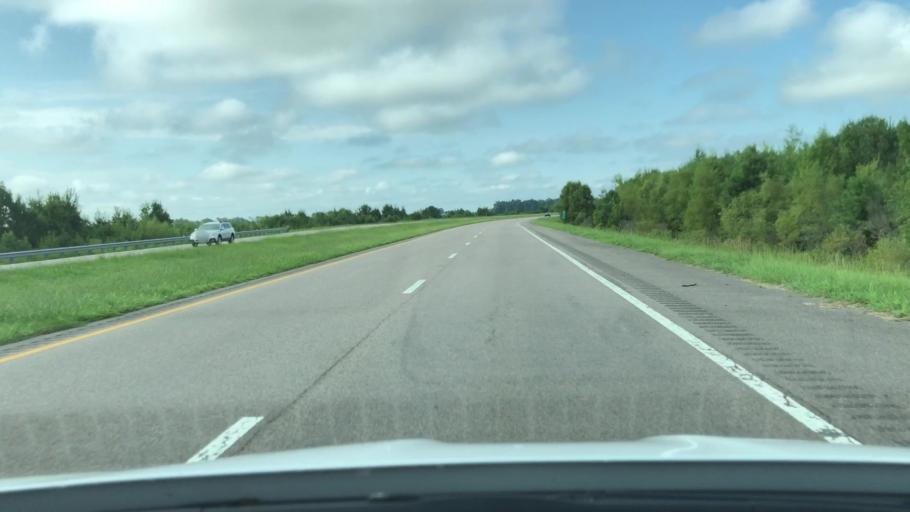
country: US
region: Virginia
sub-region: City of Portsmouth
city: Portsmouth Heights
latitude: 36.6248
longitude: -76.3653
